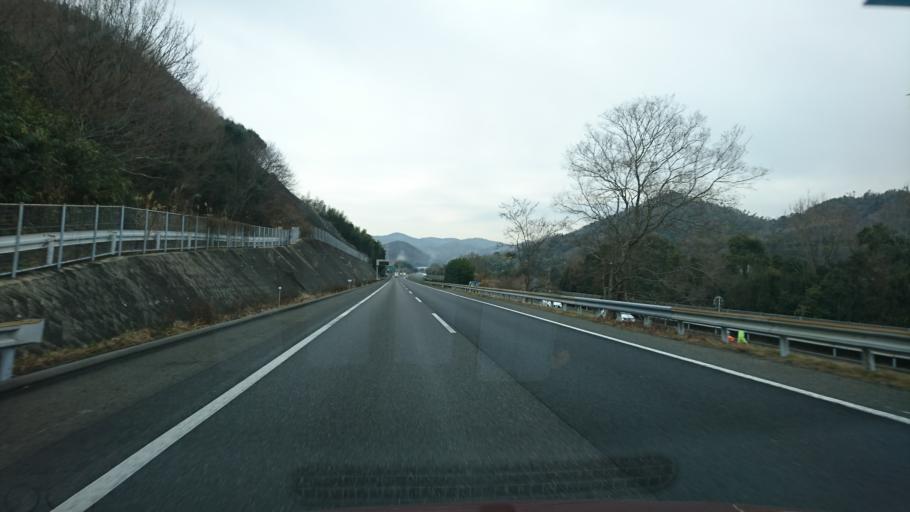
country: JP
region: Okayama
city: Kamogatacho-kamogata
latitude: 34.5528
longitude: 133.5999
